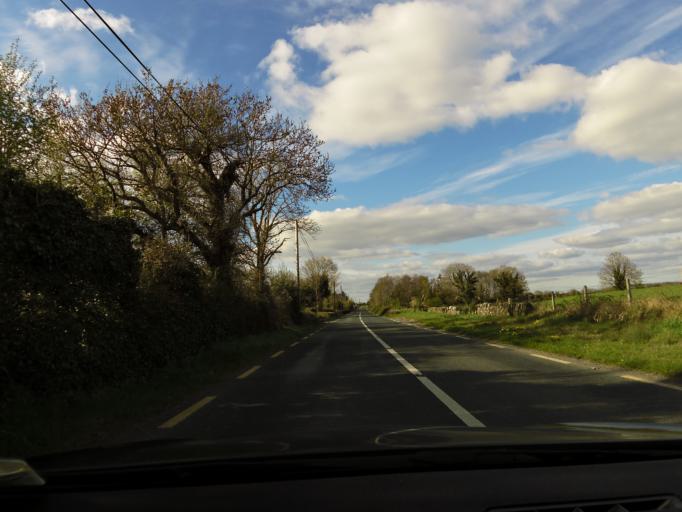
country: IE
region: Connaught
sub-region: County Galway
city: Portumna
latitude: 53.1157
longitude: -8.2391
